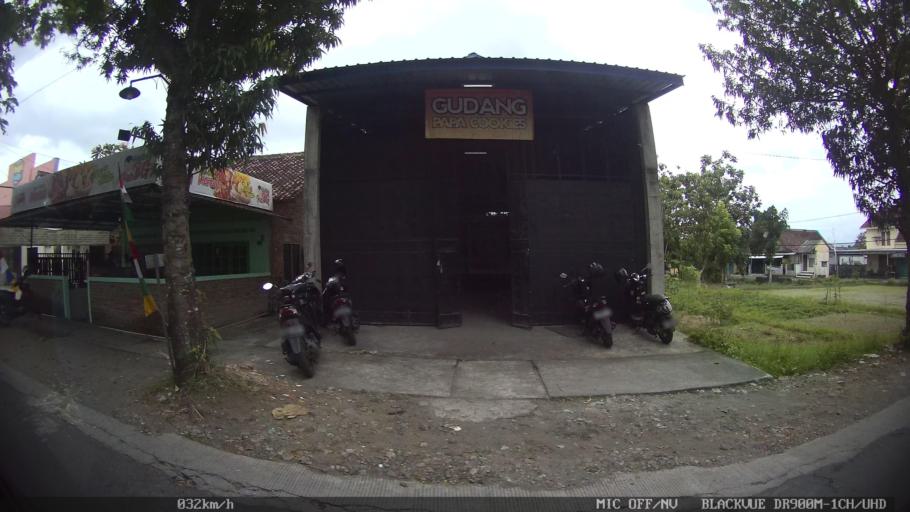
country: ID
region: Daerah Istimewa Yogyakarta
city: Depok
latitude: -7.8114
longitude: 110.4181
